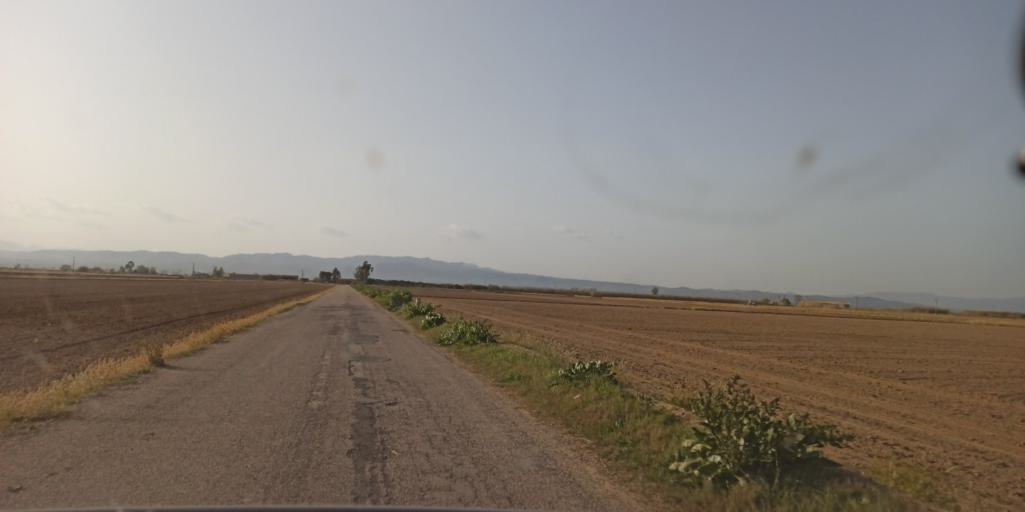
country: ES
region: Catalonia
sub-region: Provincia de Tarragona
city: Deltebre
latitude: 40.7481
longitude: 0.7654
